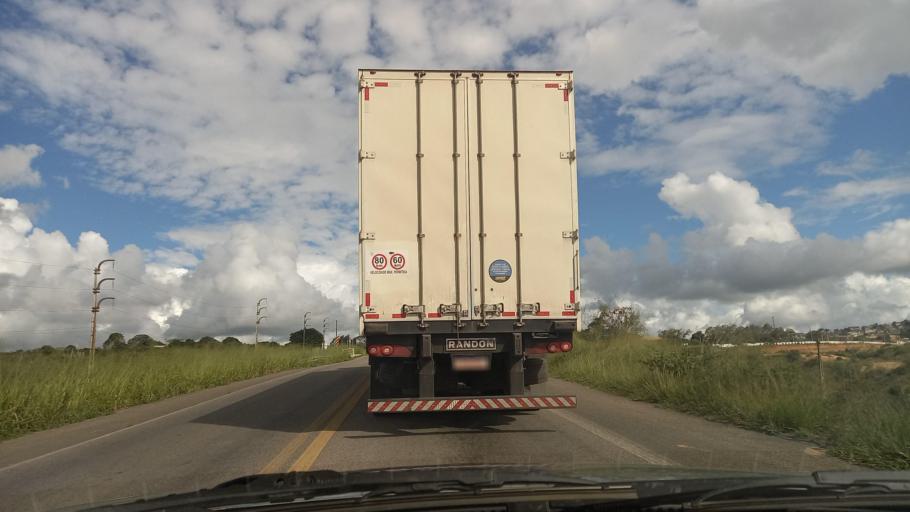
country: BR
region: Pernambuco
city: Garanhuns
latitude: -8.8637
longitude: -36.4632
